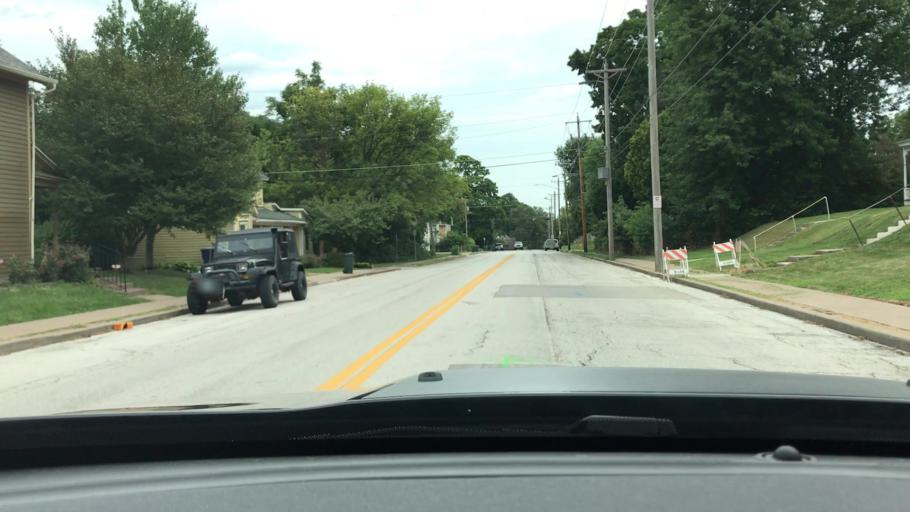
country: US
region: Iowa
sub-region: Scott County
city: Davenport
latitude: 41.5323
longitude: -90.5551
